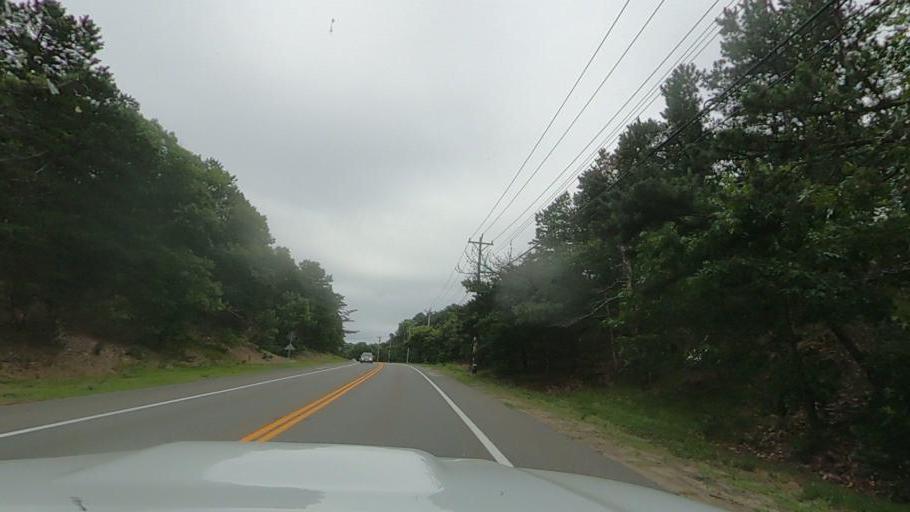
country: US
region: Massachusetts
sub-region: Barnstable County
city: Truro
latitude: 41.9831
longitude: -70.0442
